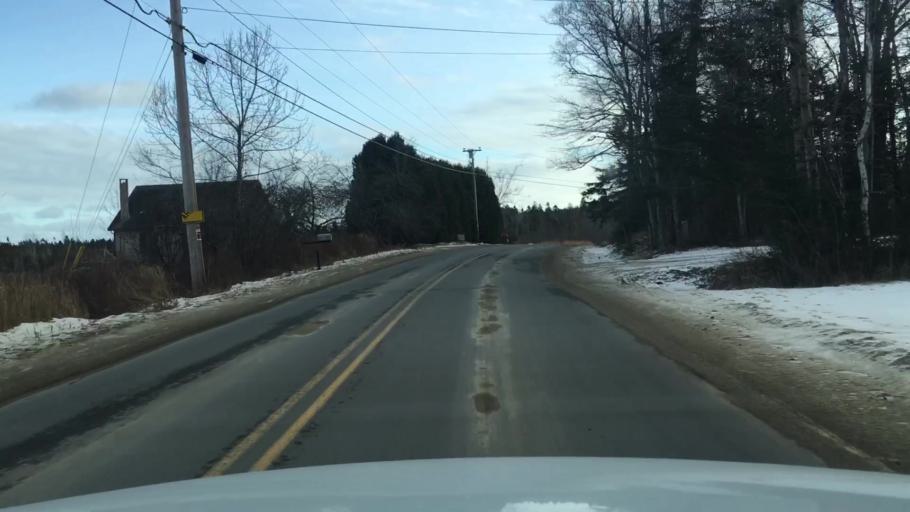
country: US
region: Maine
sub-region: Washington County
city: Jonesport
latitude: 44.6139
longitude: -67.6030
